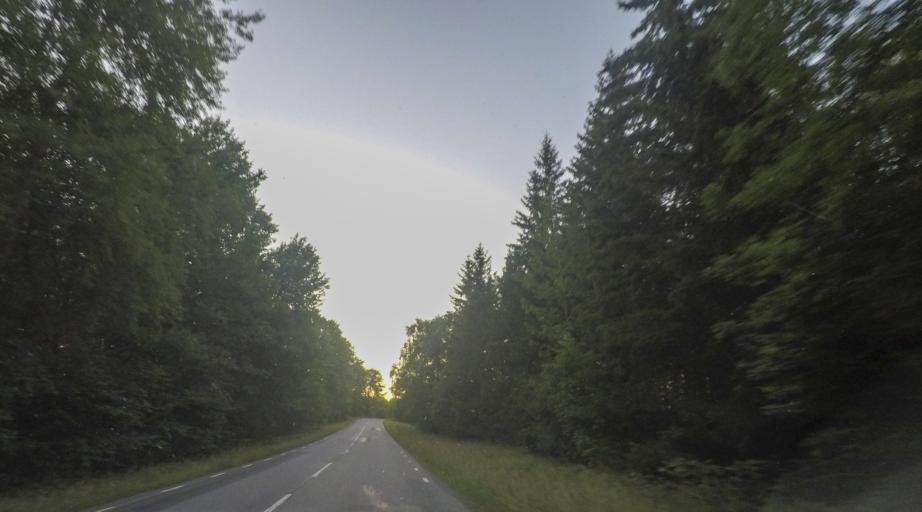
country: SE
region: Soedermanland
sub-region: Trosa Kommun
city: Trosa
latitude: 58.9799
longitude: 17.6897
